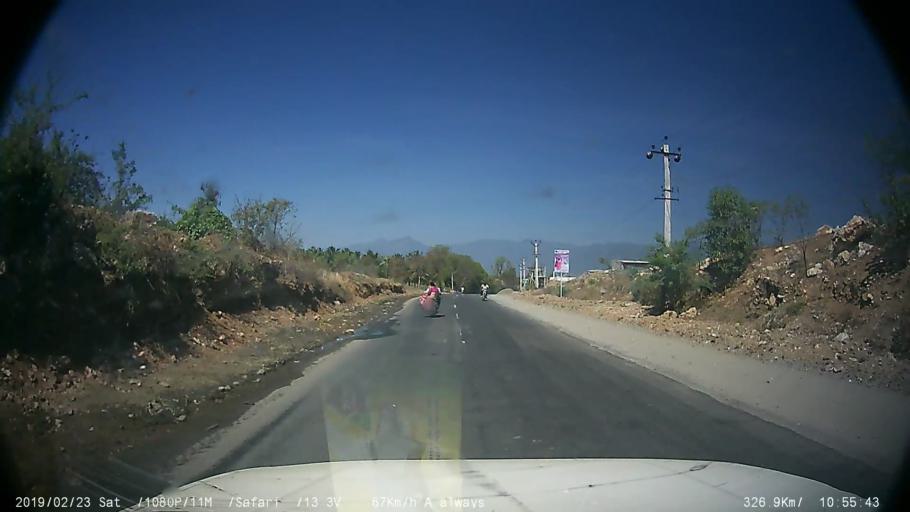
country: IN
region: Tamil Nadu
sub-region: Coimbatore
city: Sirumugai
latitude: 11.2586
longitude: 77.0358
